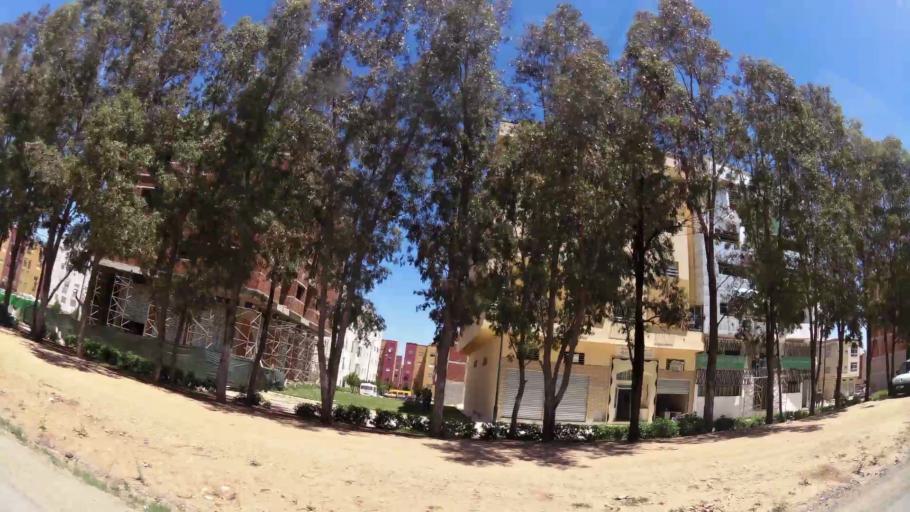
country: MA
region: Meknes-Tafilalet
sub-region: Meknes
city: Meknes
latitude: 33.8526
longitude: -5.5657
